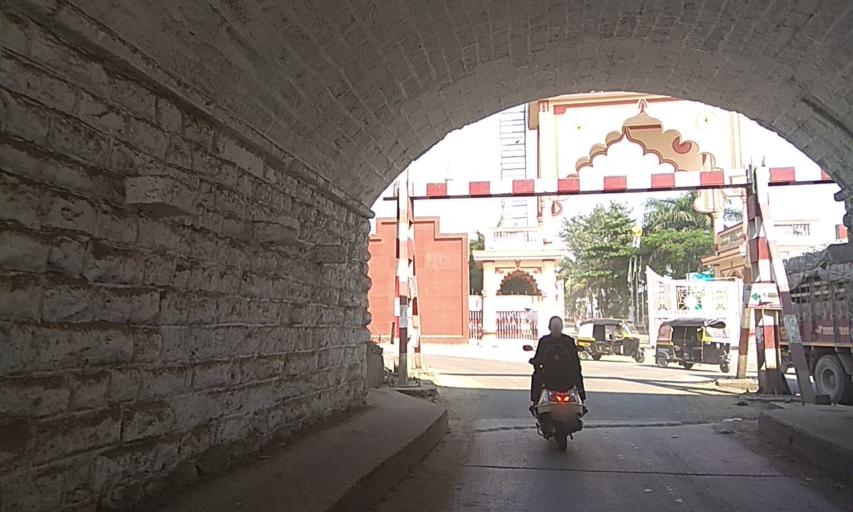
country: IN
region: Maharashtra
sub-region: Pune Division
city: Sasvad
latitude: 18.4897
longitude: 74.0254
